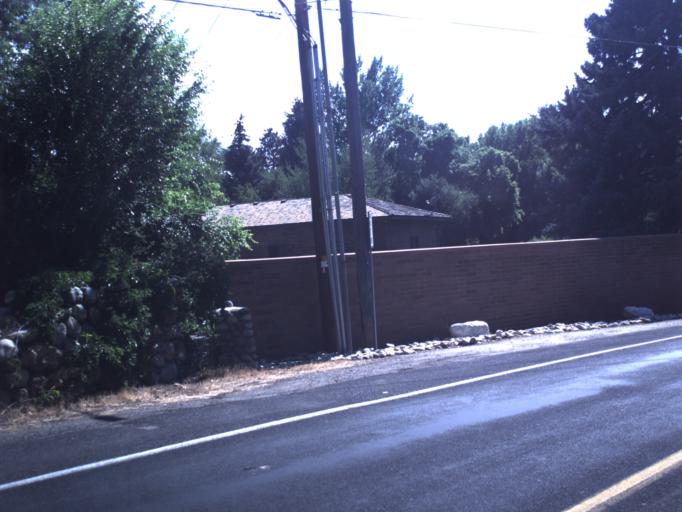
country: US
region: Utah
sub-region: Salt Lake County
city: Cottonwood Heights
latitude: 40.6379
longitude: -111.8129
